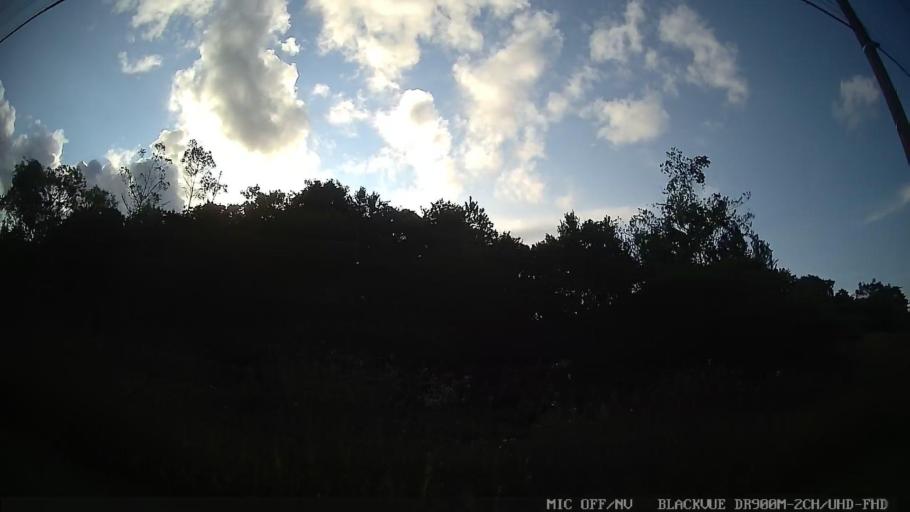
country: BR
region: Sao Paulo
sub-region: Itanhaem
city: Itanhaem
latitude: -24.1541
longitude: -46.8243
